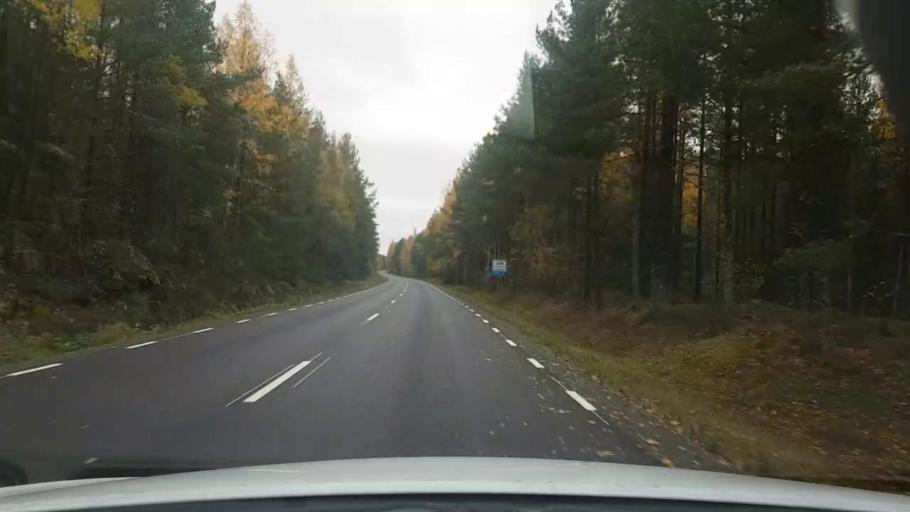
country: SE
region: OErebro
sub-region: Laxa Kommun
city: Laxa
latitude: 58.8024
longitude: 14.5426
